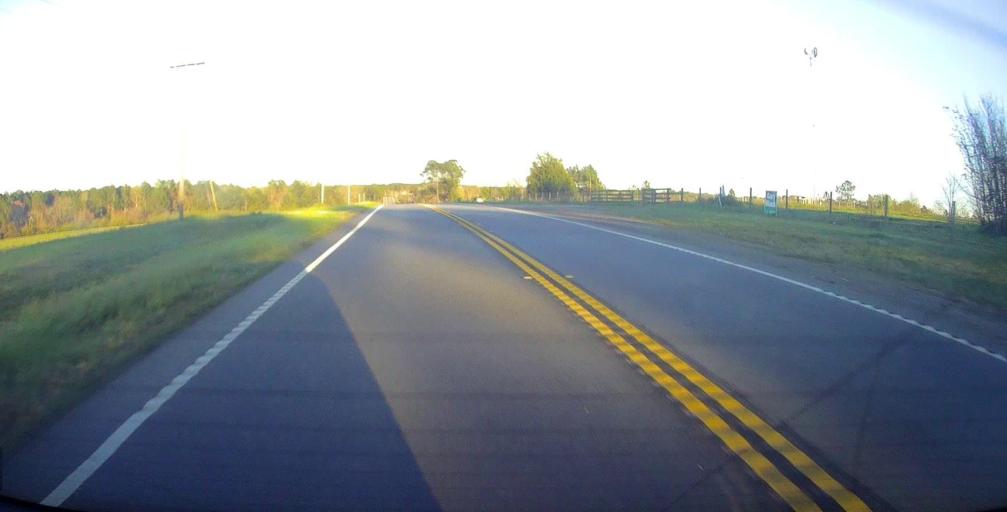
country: US
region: Georgia
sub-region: Crisp County
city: Cordele
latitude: 31.9503
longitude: -83.7118
